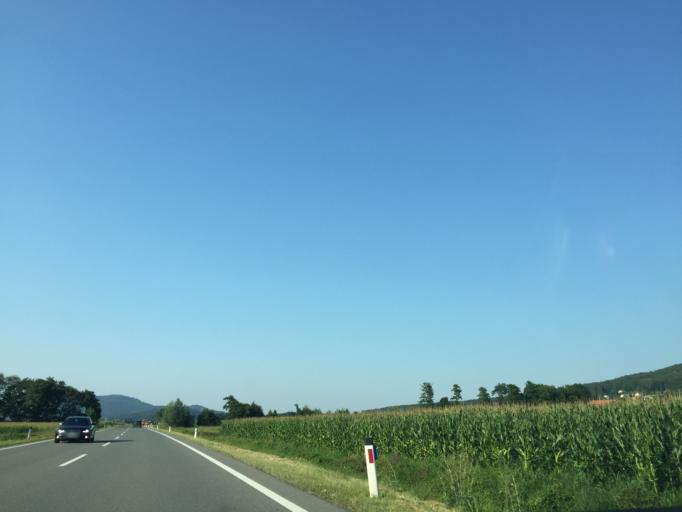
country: AT
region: Styria
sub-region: Politischer Bezirk Suedoststeiermark
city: Stainz bei Straden
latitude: 46.8368
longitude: 15.8981
